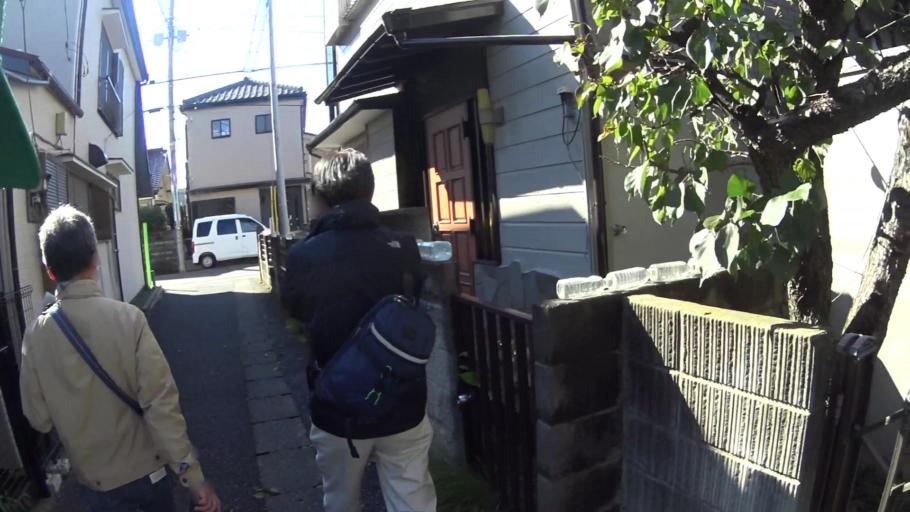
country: JP
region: Tokyo
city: Chofugaoka
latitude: 35.6461
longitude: 139.5012
